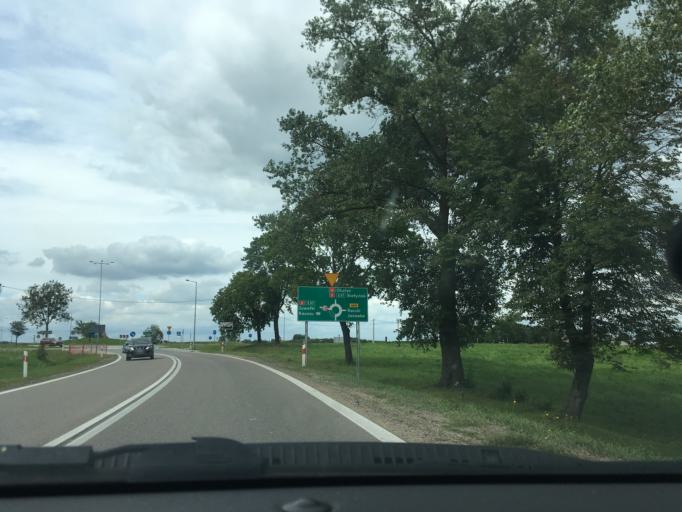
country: PL
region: Podlasie
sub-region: Powiat augustowski
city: Augustow
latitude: 53.8453
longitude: 22.9523
